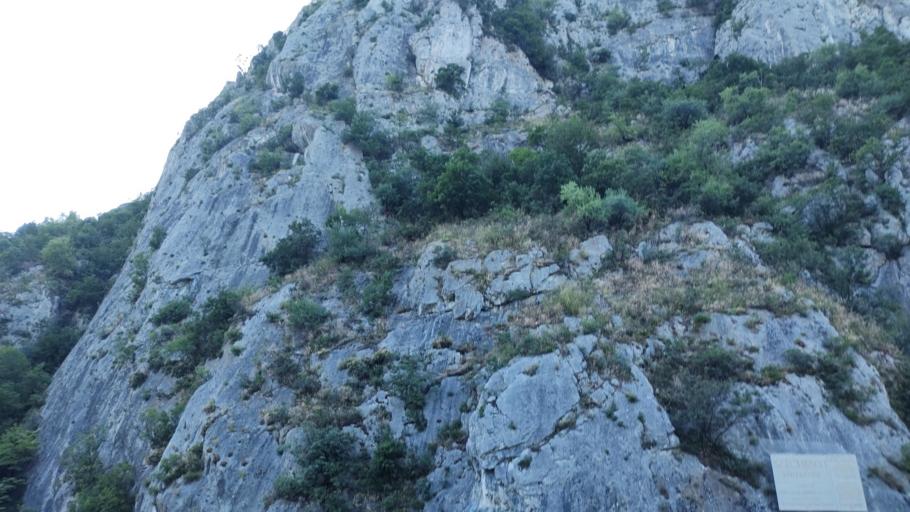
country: RO
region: Mehedinti
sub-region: Comuna Dubova
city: Dubova
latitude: 44.5899
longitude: 22.2582
